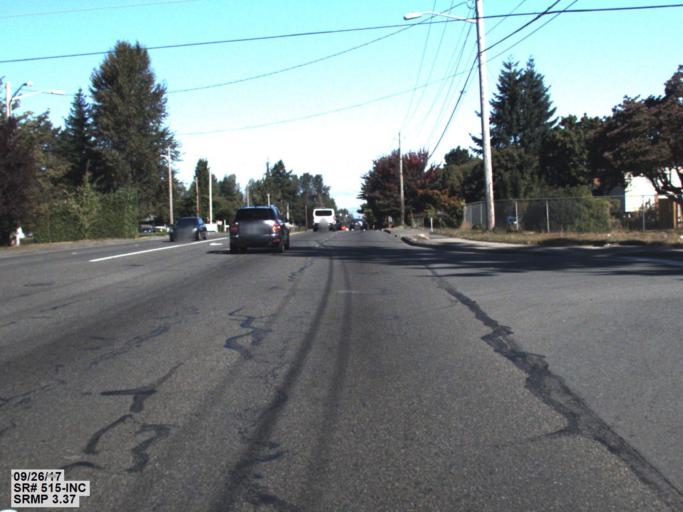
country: US
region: Washington
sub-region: King County
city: East Hill-Meridian
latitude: 47.4195
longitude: -122.1970
